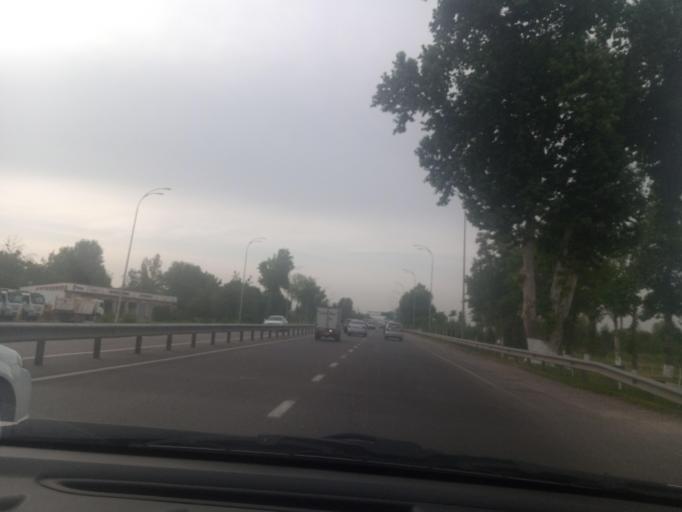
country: UZ
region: Toshkent Shahri
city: Bektemir
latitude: 41.2523
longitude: 69.3863
